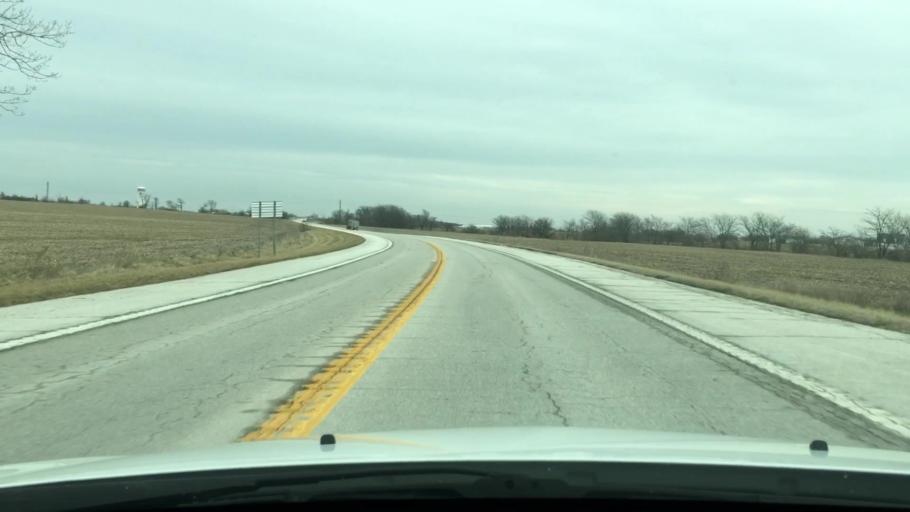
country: US
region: Missouri
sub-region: Pike County
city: Bowling Green
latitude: 39.3455
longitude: -91.2313
